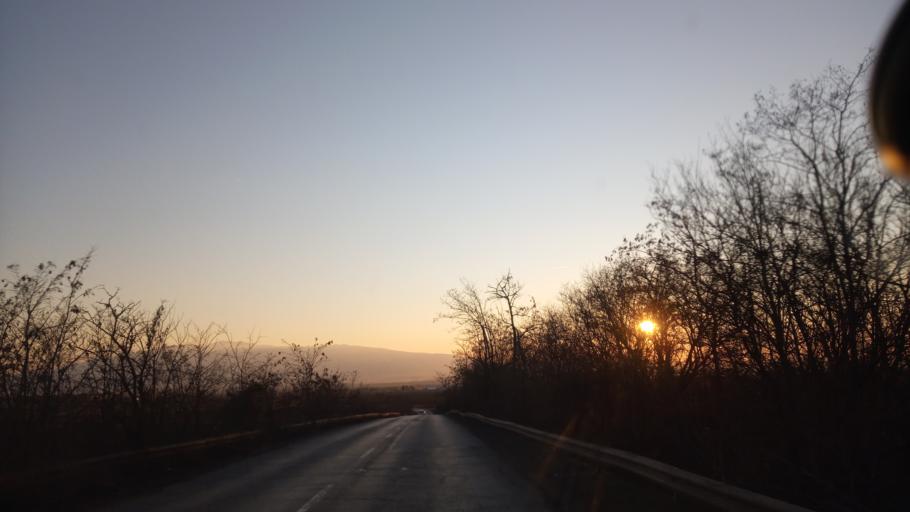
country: BG
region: Sofia-Capital
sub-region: Stolichna Obshtina
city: Bukhovo
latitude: 42.7695
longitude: 23.4959
